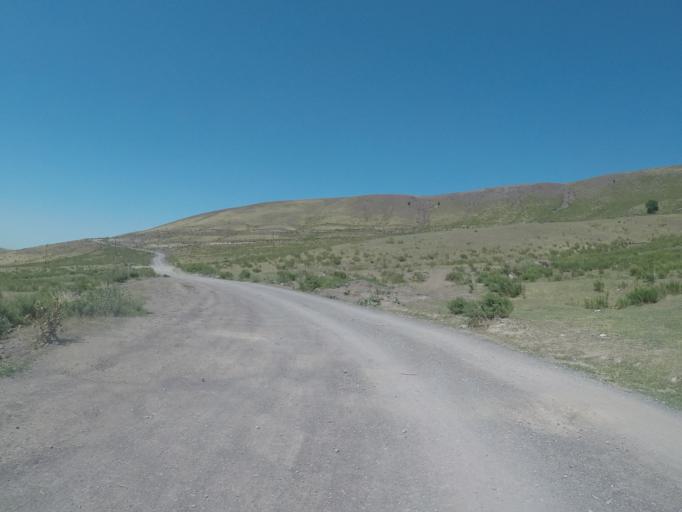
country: KG
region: Chuy
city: Bishkek
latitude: 42.6489
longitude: 74.5180
